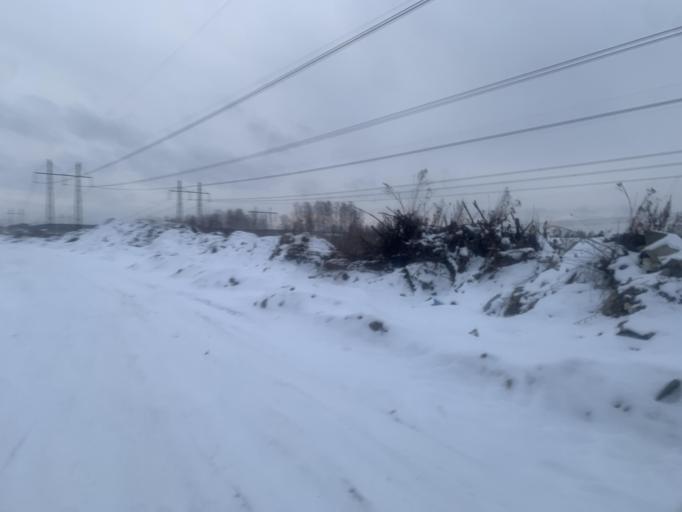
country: RU
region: Chelyabinsk
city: Roshchino
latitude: 55.1906
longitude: 61.2589
